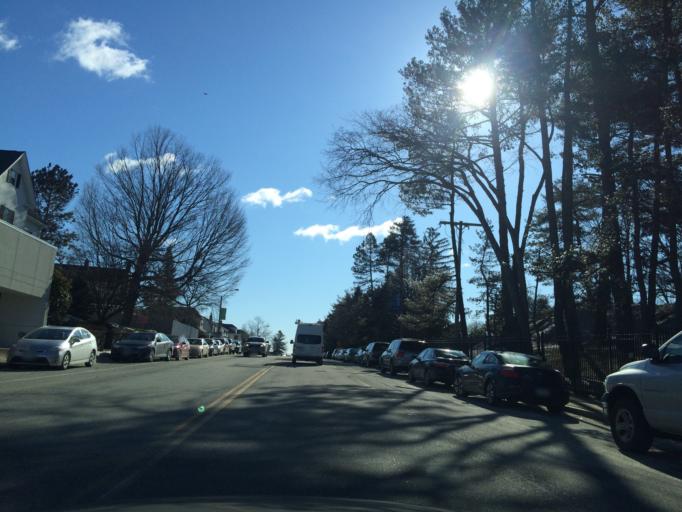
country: US
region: Massachusetts
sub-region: Middlesex County
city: Watertown
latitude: 42.3640
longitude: -71.1775
